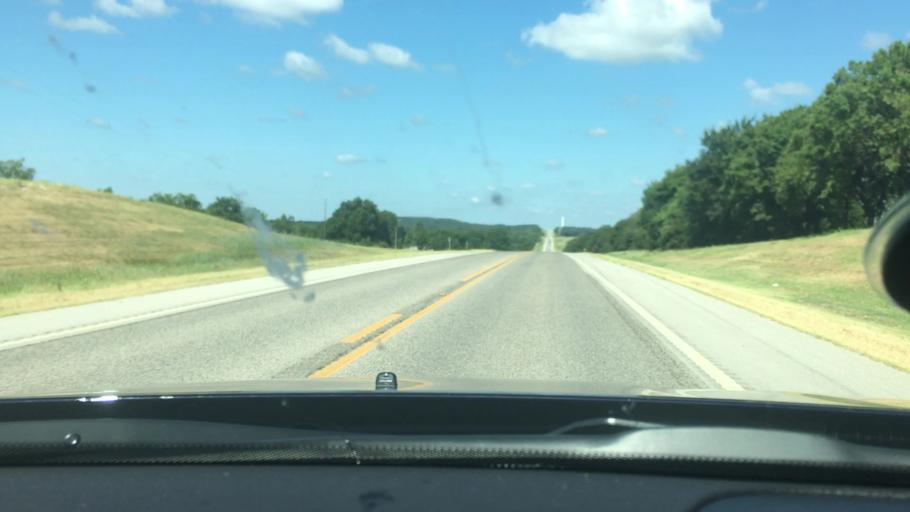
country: US
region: Oklahoma
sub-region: Carter County
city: Dickson
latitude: 34.1002
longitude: -96.9121
